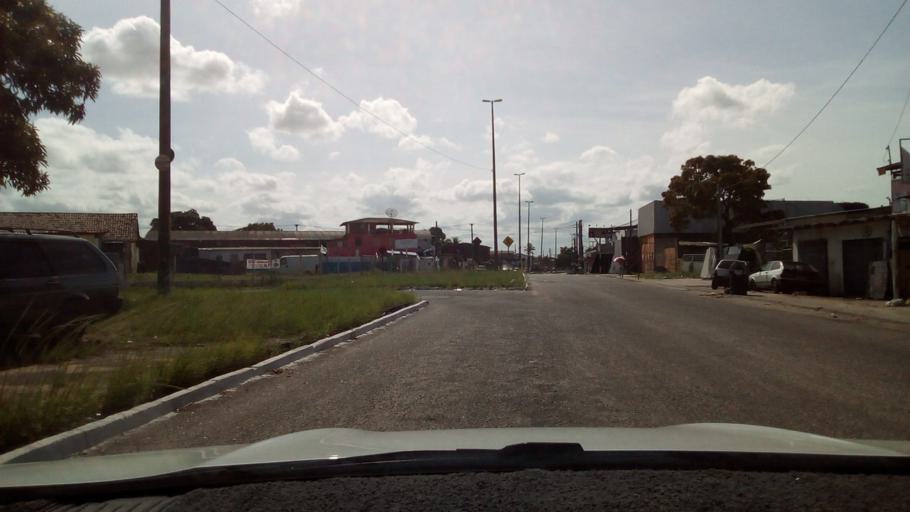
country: BR
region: Paraiba
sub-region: Joao Pessoa
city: Joao Pessoa
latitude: -7.1236
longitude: -34.8963
